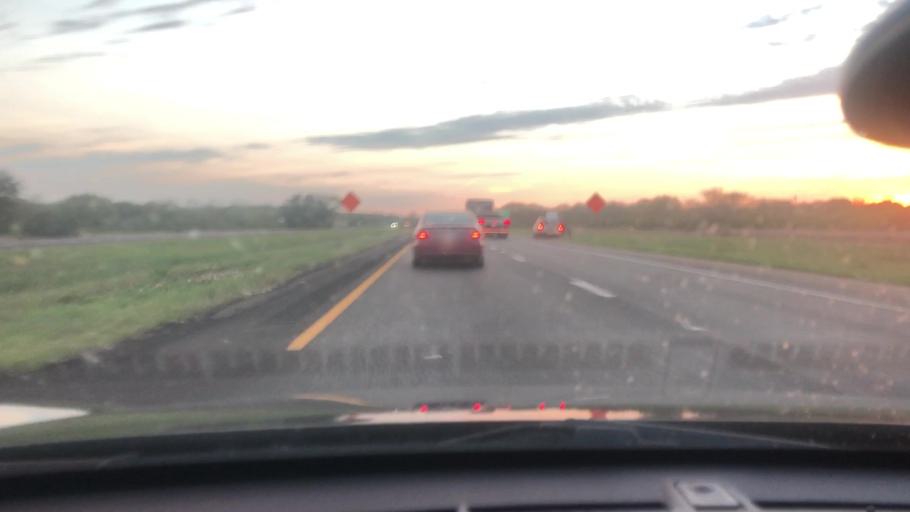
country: US
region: Texas
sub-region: Victoria County
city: Inez
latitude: 28.9157
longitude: -96.7692
